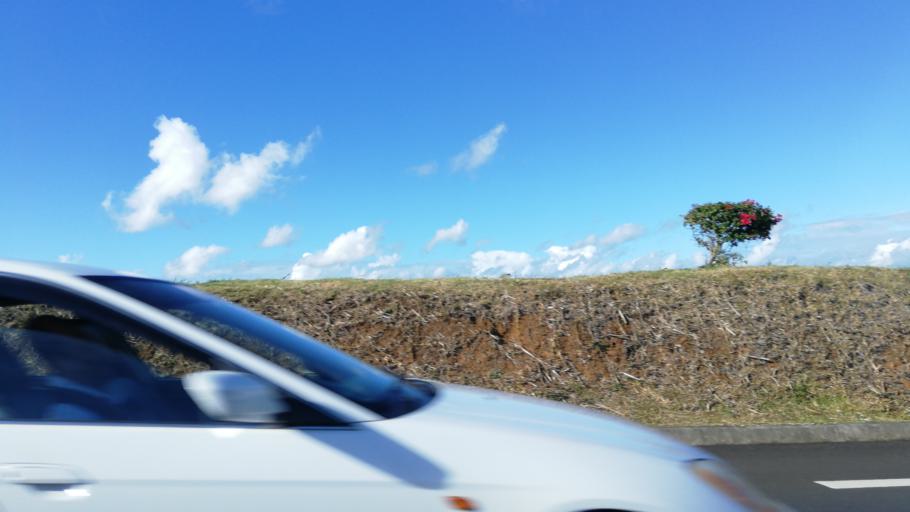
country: MU
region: Moka
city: Saint Pierre
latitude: -20.2337
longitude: 57.5127
